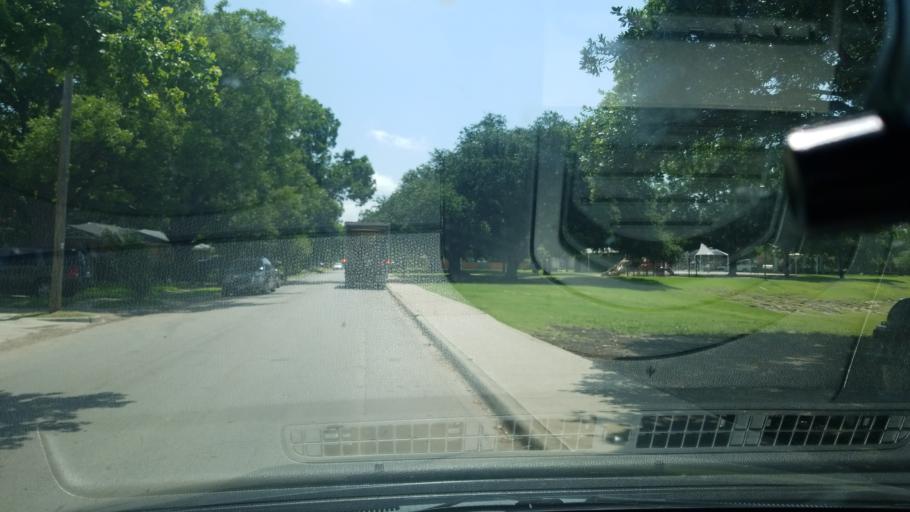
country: US
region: Texas
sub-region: Dallas County
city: Balch Springs
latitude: 32.7445
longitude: -96.6907
